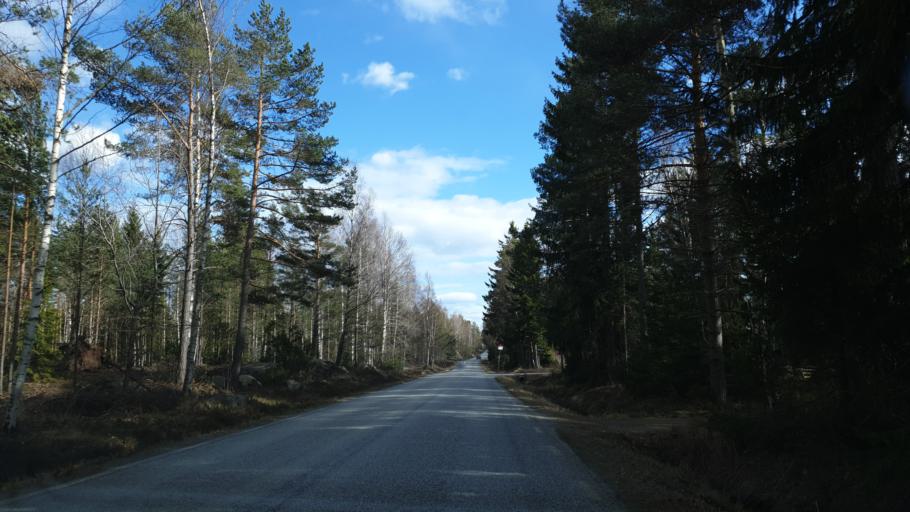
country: SE
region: Stockholm
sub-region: Varmdo Kommun
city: Mortnas
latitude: 59.2463
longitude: 18.4628
